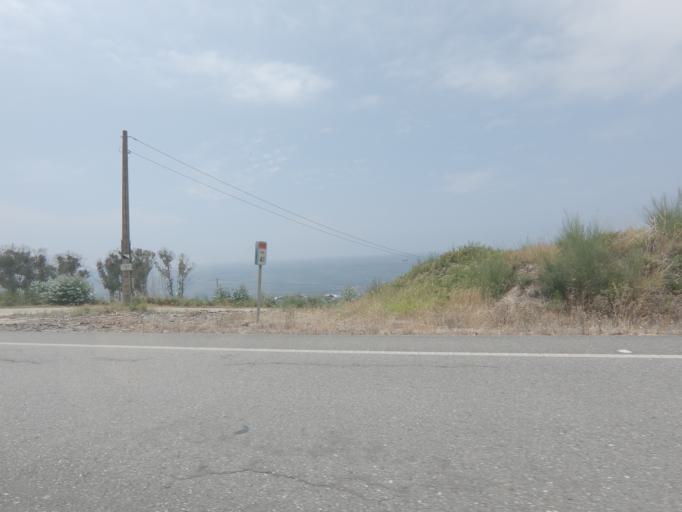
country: ES
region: Galicia
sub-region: Provincia de Pontevedra
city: A Guarda
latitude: 41.9444
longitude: -8.8818
